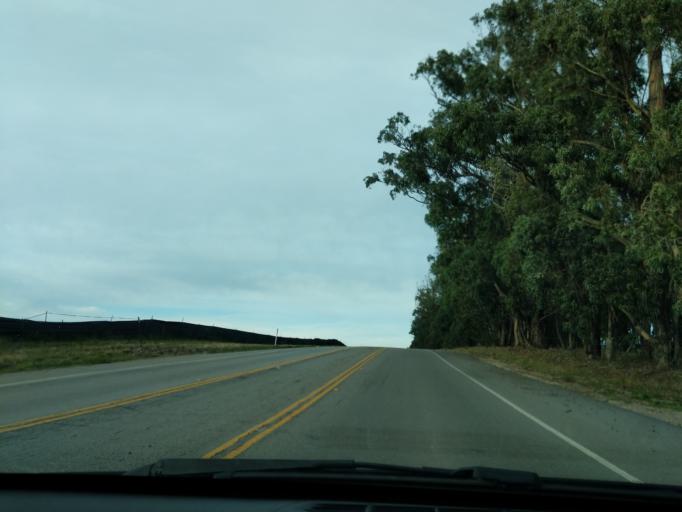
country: US
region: California
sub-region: San Luis Obispo County
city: Callender
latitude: 35.0284
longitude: -120.5611
